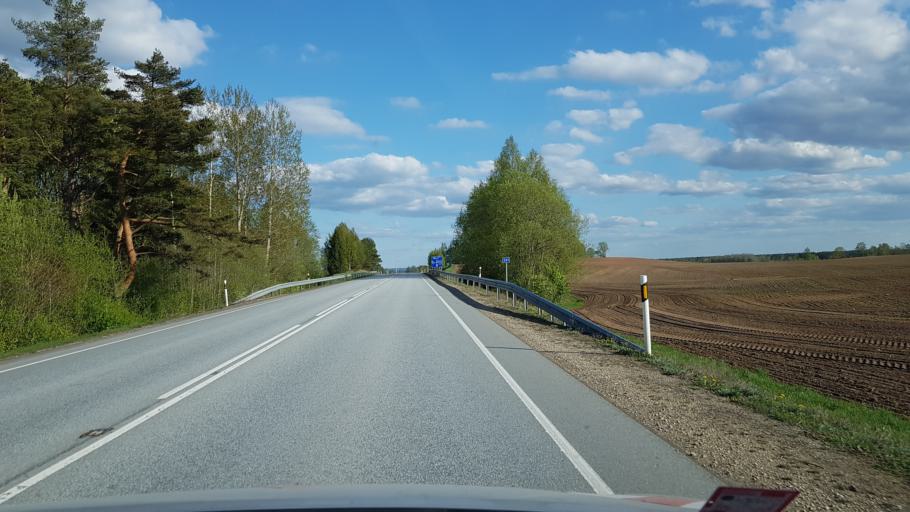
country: EE
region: Vorumaa
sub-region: Voru linn
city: Voru
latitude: 57.8958
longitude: 26.8442
